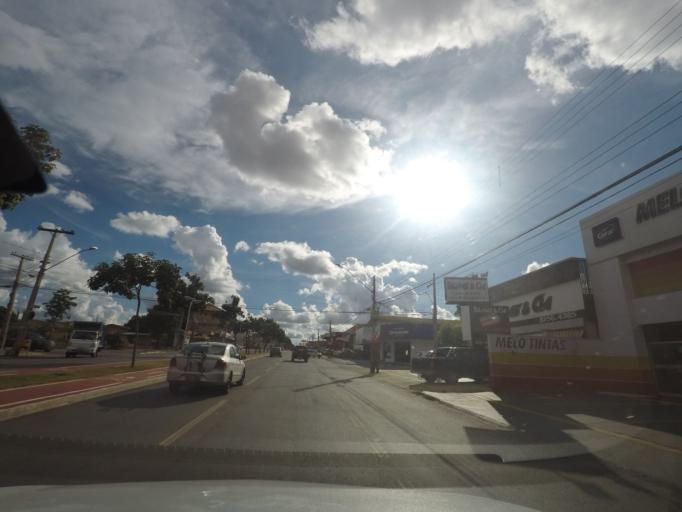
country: BR
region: Goias
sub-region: Goiania
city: Goiania
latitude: -16.7192
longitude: -49.2984
